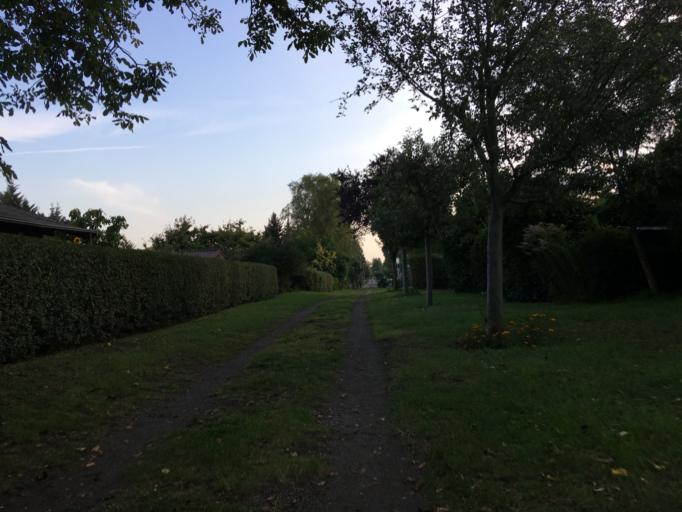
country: DE
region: Berlin
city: Biesdorf
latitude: 52.4908
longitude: 13.5546
